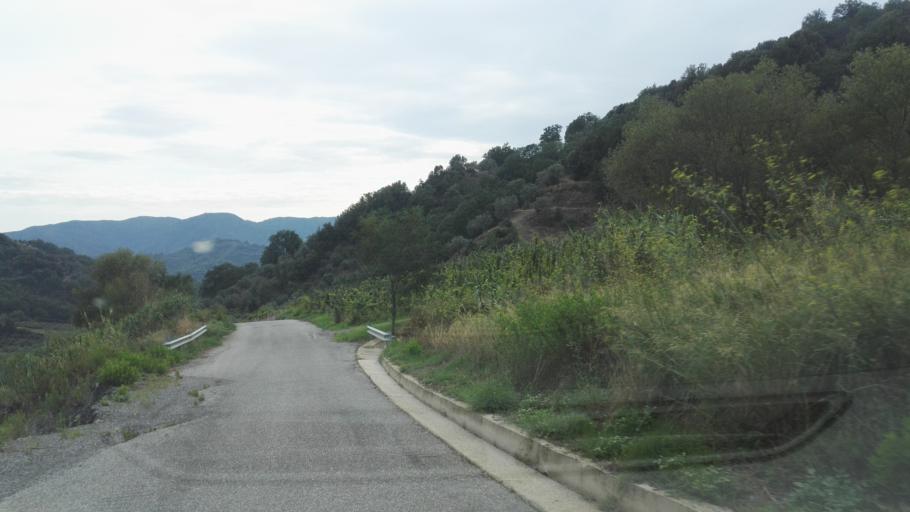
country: IT
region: Calabria
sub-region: Provincia di Reggio Calabria
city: Caulonia
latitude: 38.4324
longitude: 16.3948
